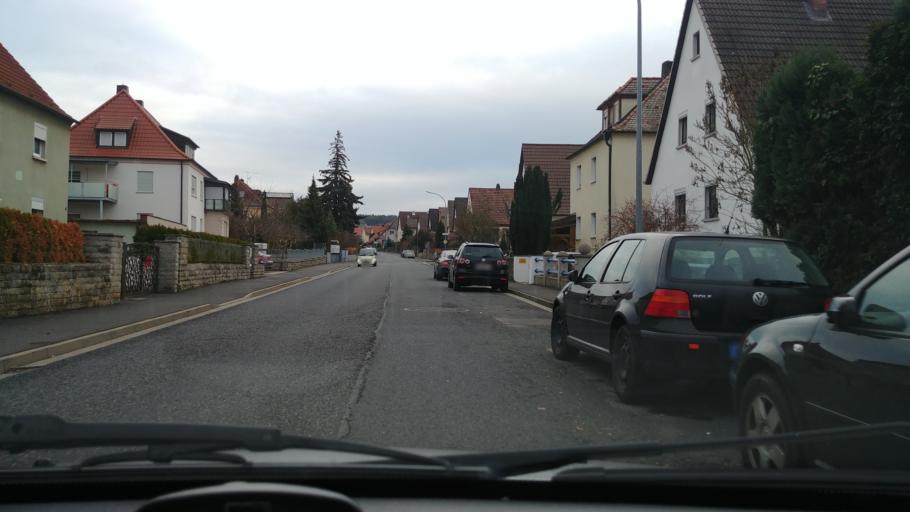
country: DE
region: Bavaria
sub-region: Regierungsbezirk Unterfranken
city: Karlstadt
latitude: 49.9584
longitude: 9.7715
